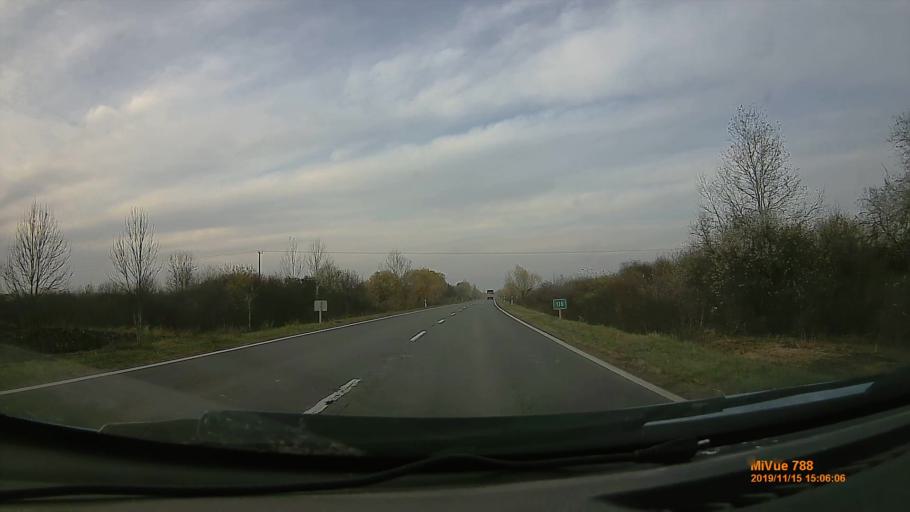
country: HU
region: Bekes
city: Gyula
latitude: 46.6392
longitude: 21.2479
